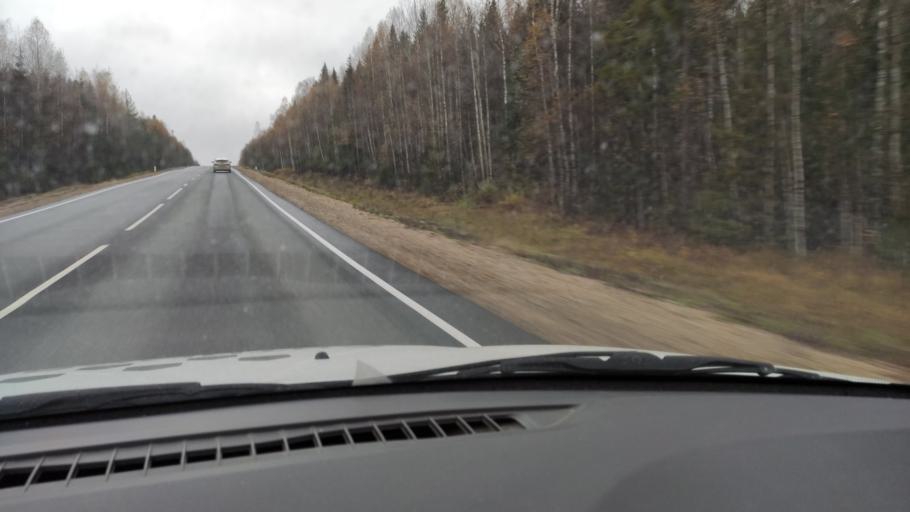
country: RU
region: Kirov
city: Chernaya Kholunitsa
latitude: 58.8591
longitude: 51.6851
